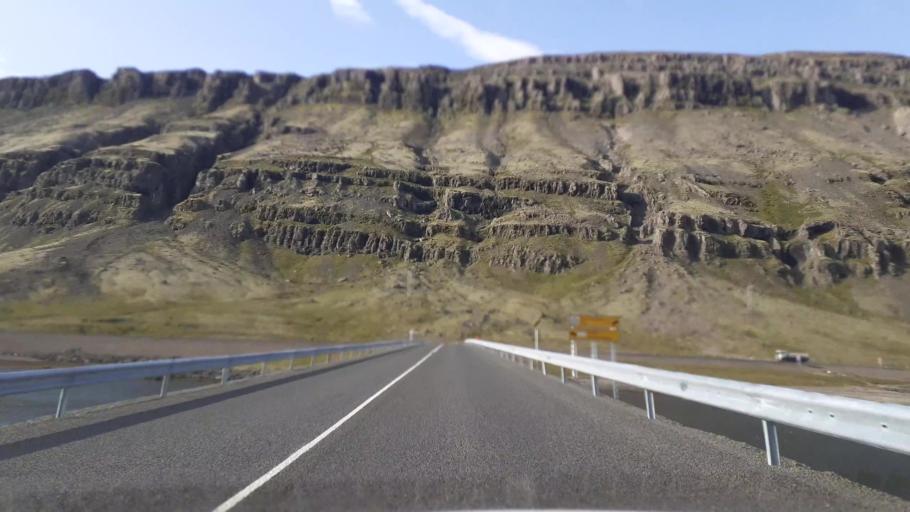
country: IS
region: East
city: Reydarfjoerdur
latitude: 64.7873
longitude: -14.4908
